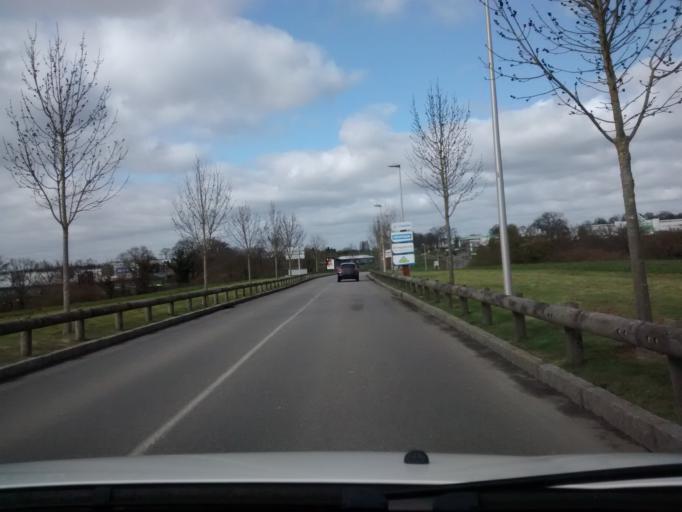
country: FR
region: Brittany
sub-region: Departement d'Ille-et-Vilaine
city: Betton
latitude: 48.1597
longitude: -1.6360
